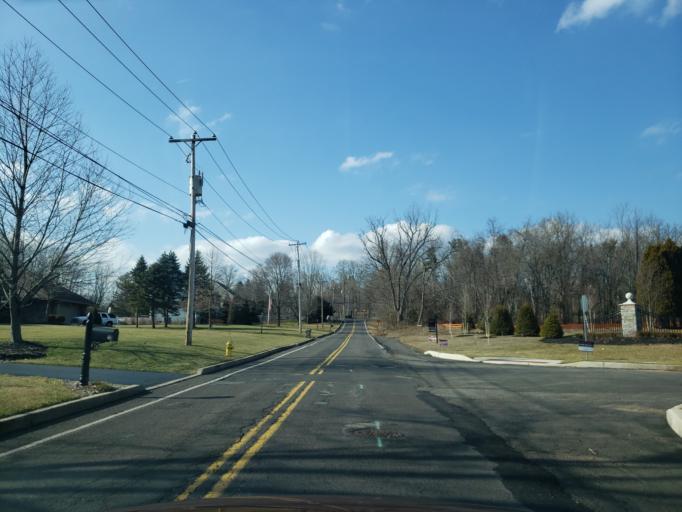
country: US
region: Pennsylvania
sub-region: Bucks County
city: Doylestown
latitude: 40.2943
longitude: -75.1461
